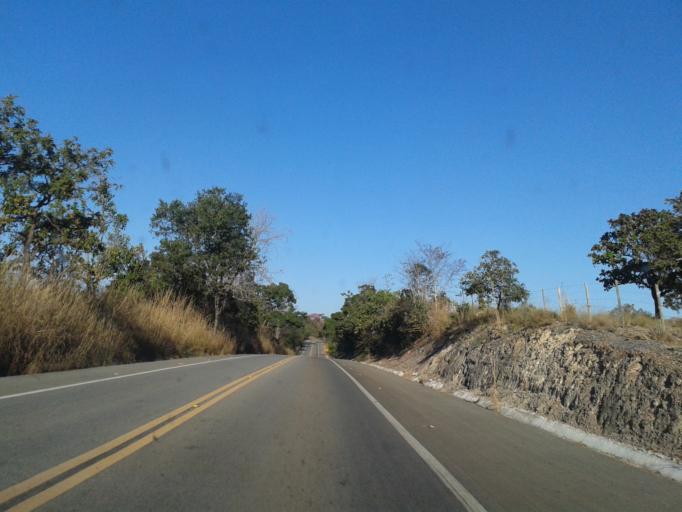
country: BR
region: Goias
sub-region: Itapuranga
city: Itapuranga
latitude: -15.5845
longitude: -50.2665
